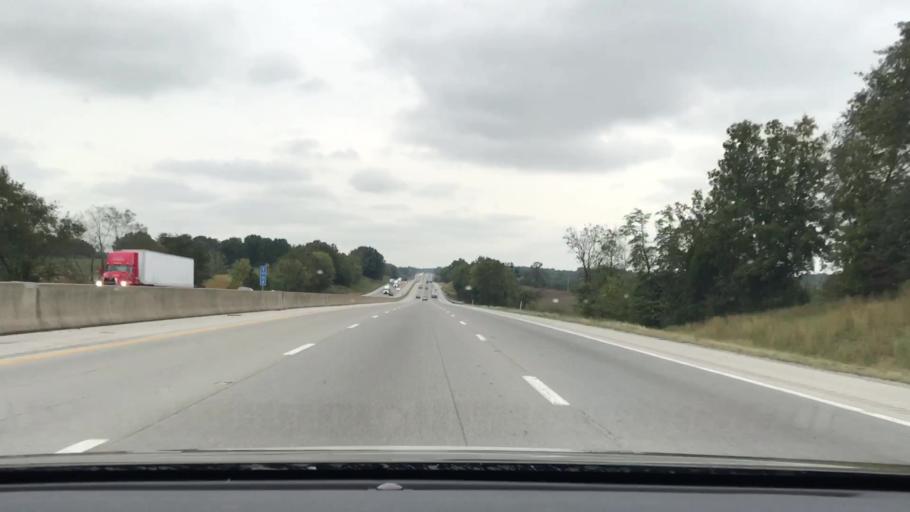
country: US
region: Kentucky
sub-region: Warren County
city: Plano
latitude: 36.7839
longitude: -86.4771
